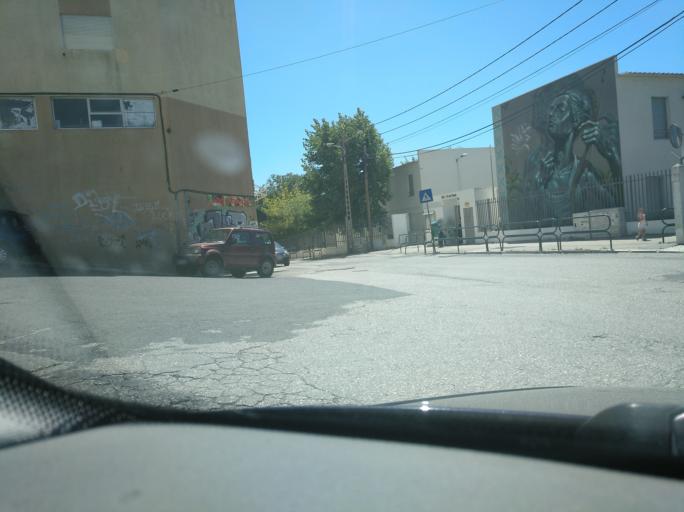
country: PT
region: Lisbon
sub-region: Loures
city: Camarate
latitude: 38.8025
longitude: -9.1445
